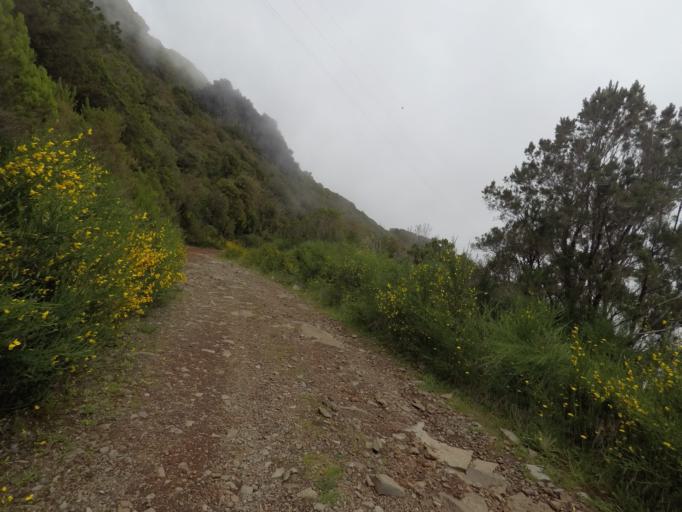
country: PT
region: Madeira
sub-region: Sao Vicente
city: Sao Vicente
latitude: 32.7690
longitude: -17.0674
